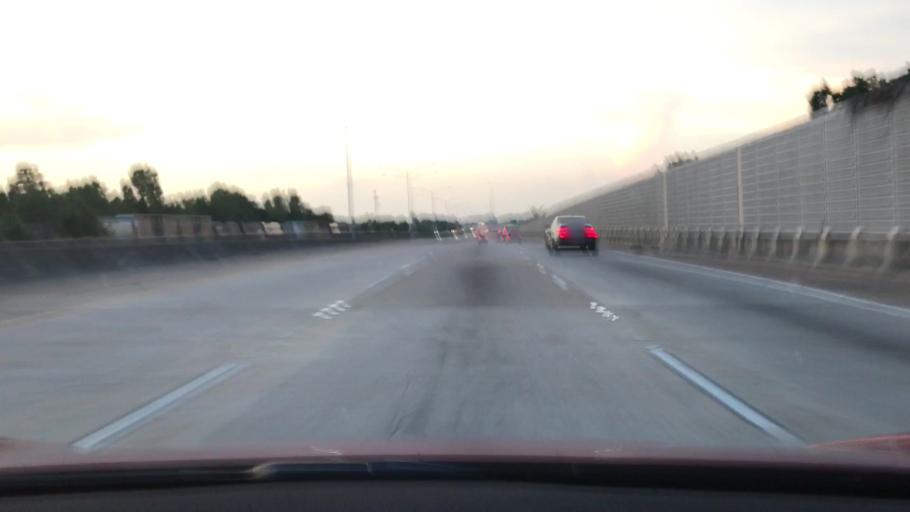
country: US
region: Louisiana
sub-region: Bossier Parish
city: Bossier City
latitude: 32.4694
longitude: -93.7552
